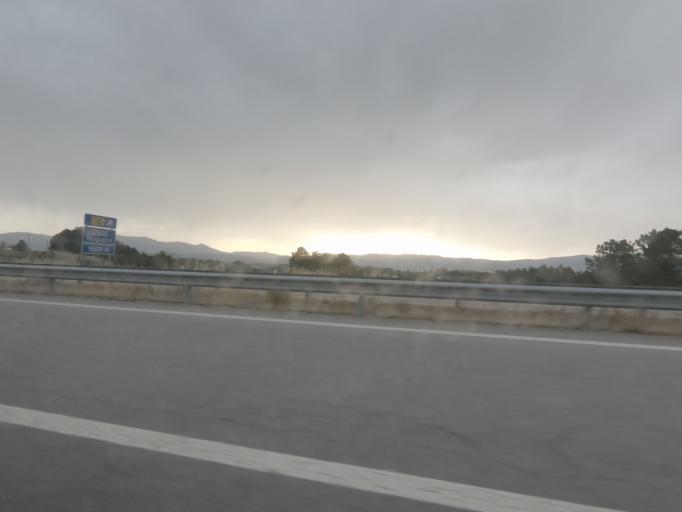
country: PT
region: Vila Real
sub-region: Vila Real
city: Vila Real
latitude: 41.2681
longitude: -7.6994
